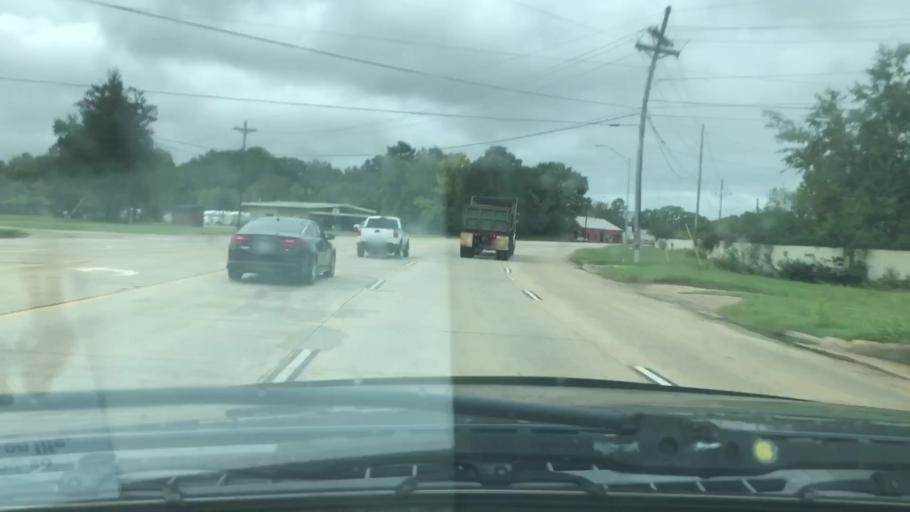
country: US
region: Texas
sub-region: Bowie County
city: Texarkana
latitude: 33.4225
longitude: -94.0713
